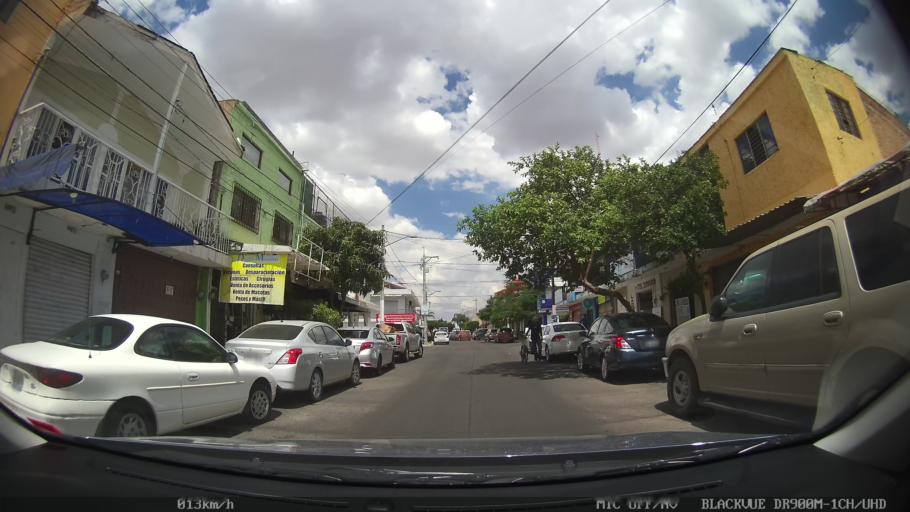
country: MX
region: Jalisco
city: Tlaquepaque
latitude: 20.6510
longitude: -103.2809
